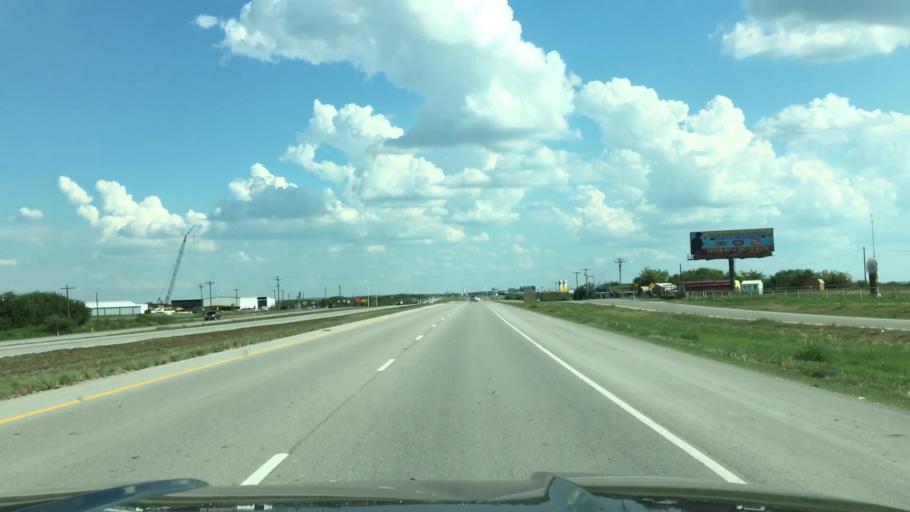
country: US
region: Texas
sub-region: Wise County
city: Decatur
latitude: 33.1999
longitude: -97.5640
